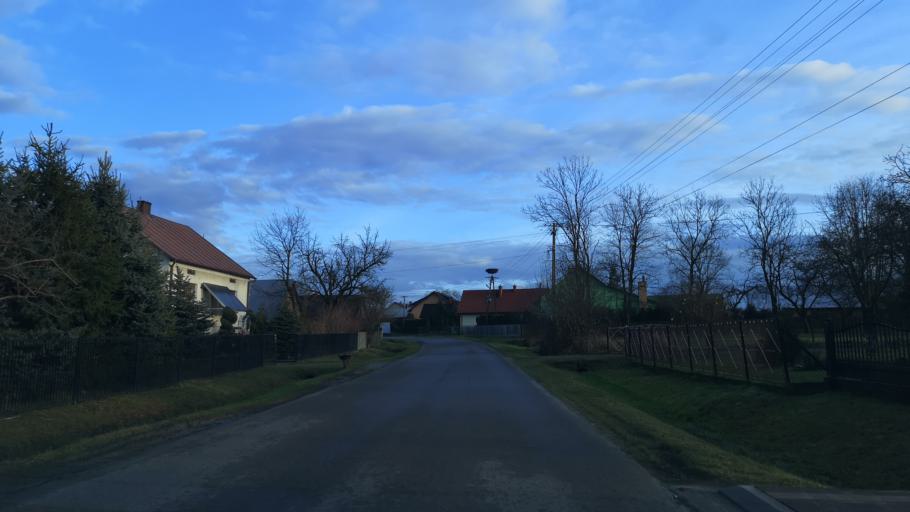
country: PL
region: Subcarpathian Voivodeship
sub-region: Powiat przeworski
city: Sieniawa
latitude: 50.2539
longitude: 22.6158
